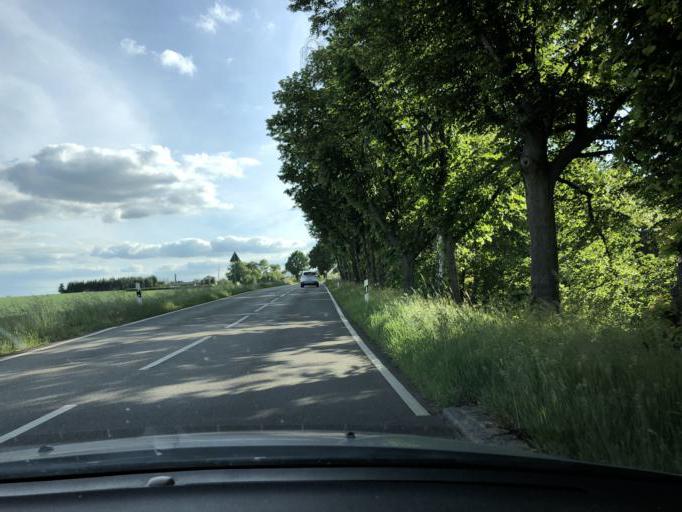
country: DE
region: Thuringia
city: Gossnitz
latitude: 50.8896
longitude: 12.4222
